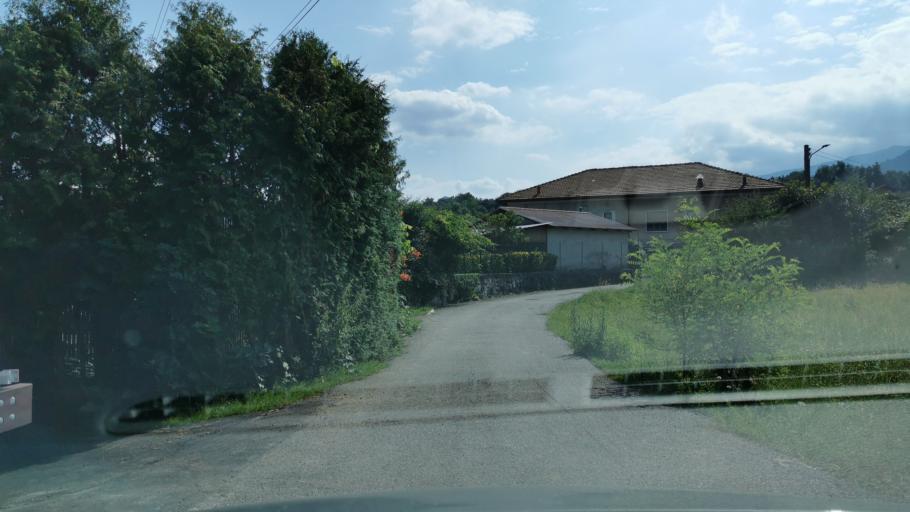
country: IT
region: Piedmont
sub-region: Provincia di Torino
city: Fiano
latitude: 45.2341
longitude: 7.5299
